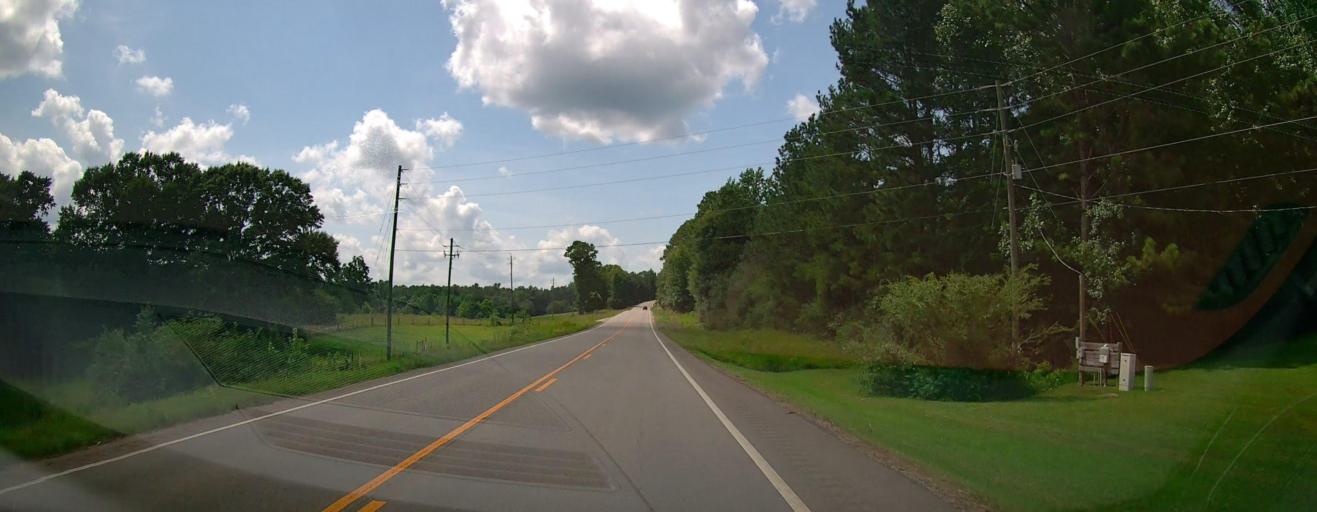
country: US
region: Alabama
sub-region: Cleburne County
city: Heflin
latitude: 33.5817
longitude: -85.4695
